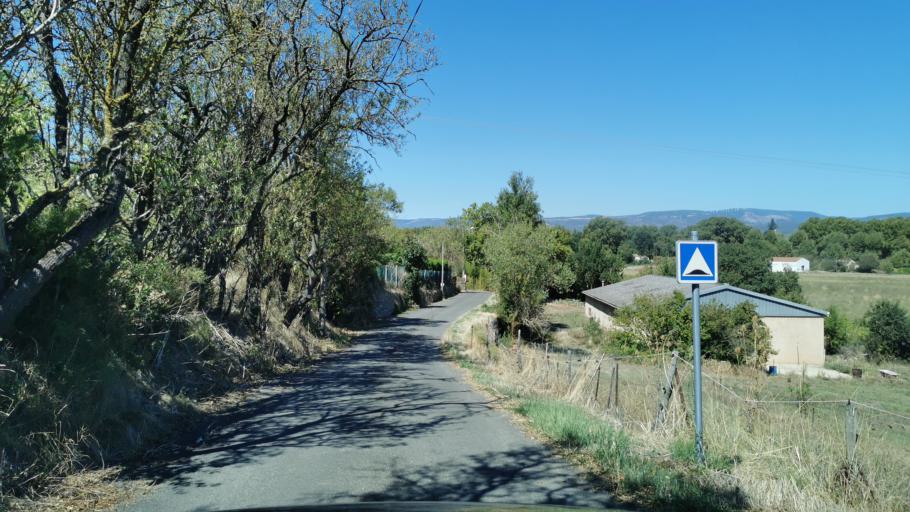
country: FR
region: Languedoc-Roussillon
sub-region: Departement de l'Aude
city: Conques-sur-Orbiel
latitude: 43.2505
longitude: 2.4086
